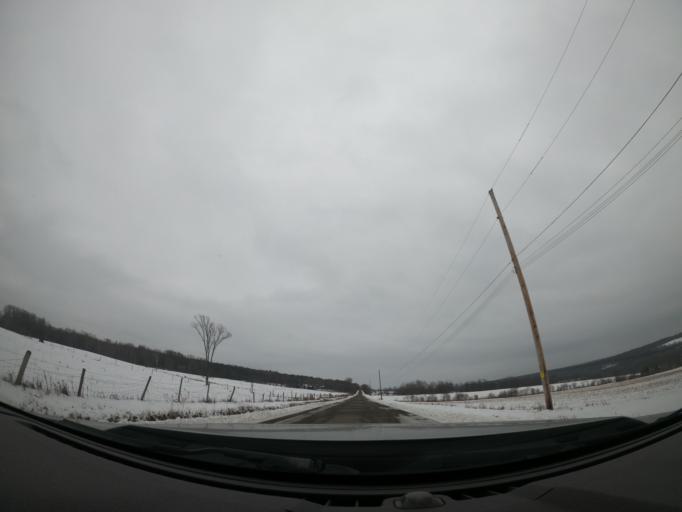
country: US
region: New York
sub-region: Cortland County
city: Homer
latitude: 42.7217
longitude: -76.2789
